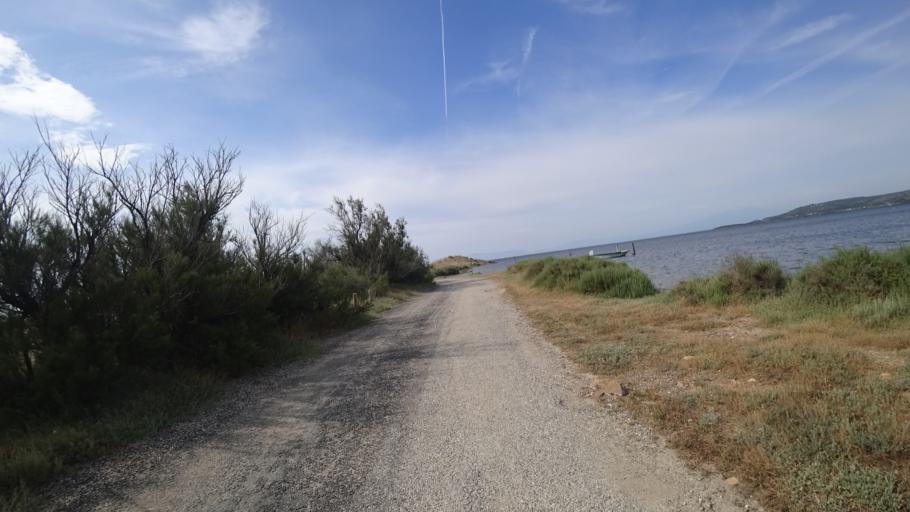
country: FR
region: Languedoc-Roussillon
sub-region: Departement de l'Aude
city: Leucate
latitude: 42.8967
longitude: 3.0291
